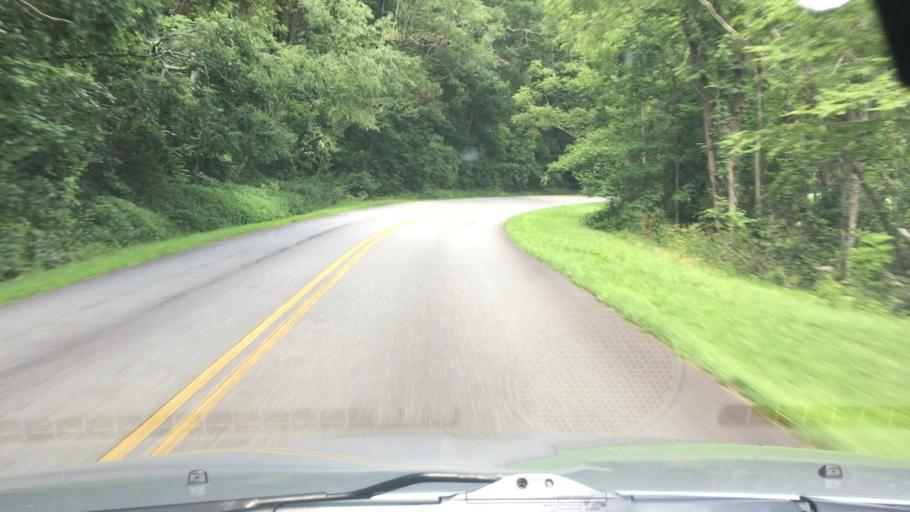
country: US
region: North Carolina
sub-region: Buncombe County
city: Weaverville
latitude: 35.6626
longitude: -82.4795
